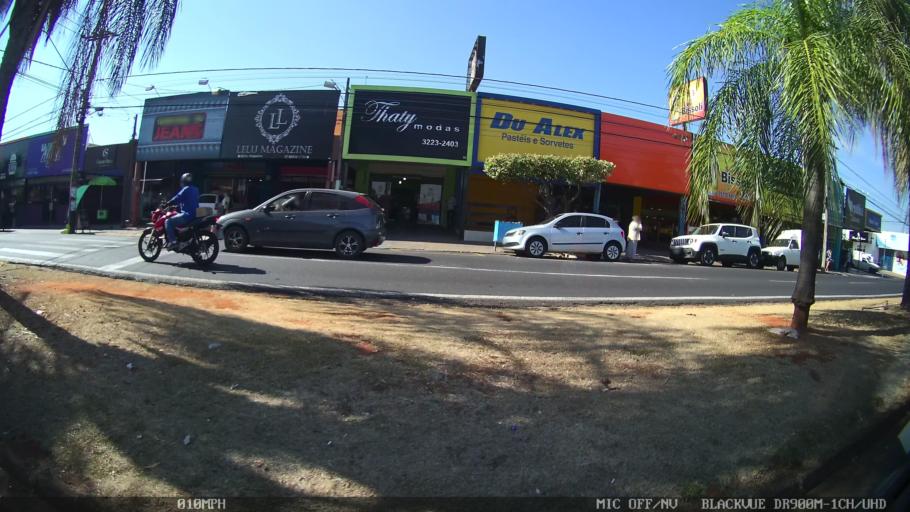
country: BR
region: Sao Paulo
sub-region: Sao Jose Do Rio Preto
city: Sao Jose do Rio Preto
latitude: -20.7803
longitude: -49.3677
